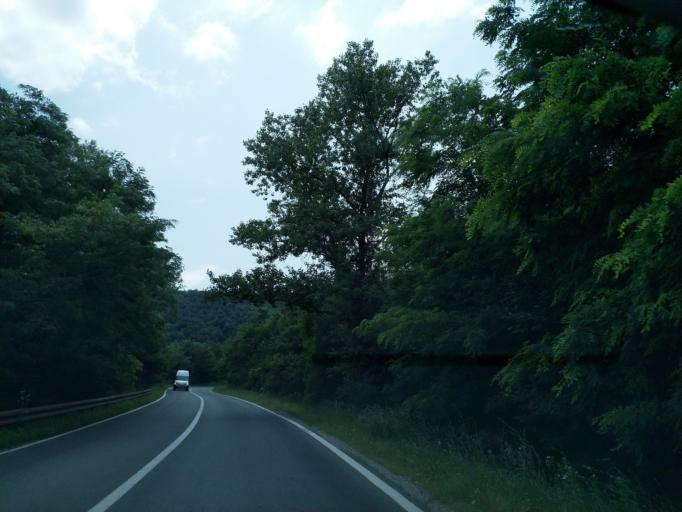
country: RS
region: Central Serbia
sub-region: Toplicki Okrug
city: Blace
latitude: 43.4159
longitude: 21.1991
